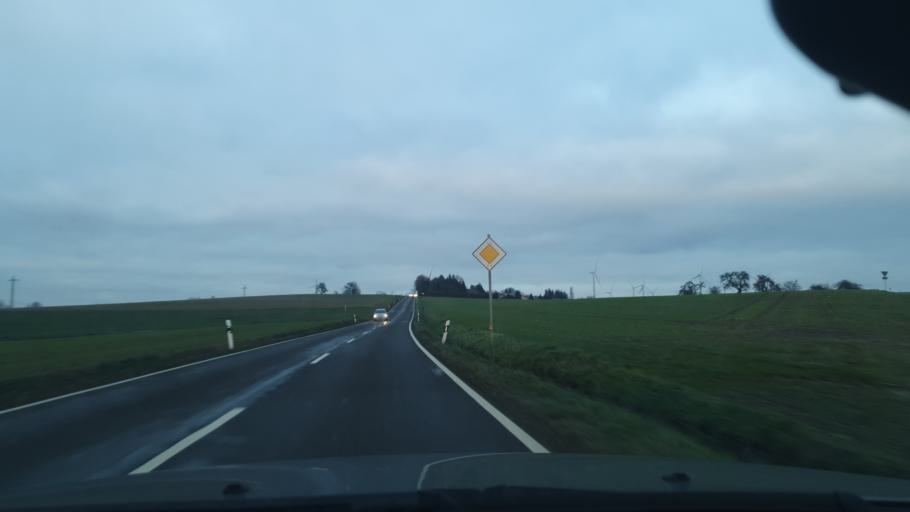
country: DE
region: Rheinland-Pfalz
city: Rosenkopf
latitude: 49.3400
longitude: 7.4289
